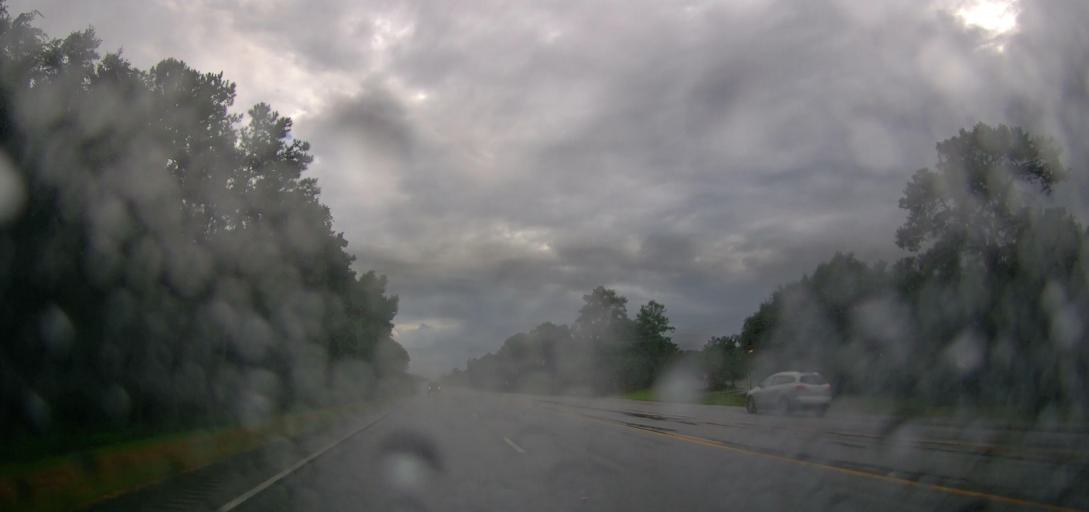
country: US
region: Georgia
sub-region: Ware County
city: Sunnyside
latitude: 31.2405
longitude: -82.3204
